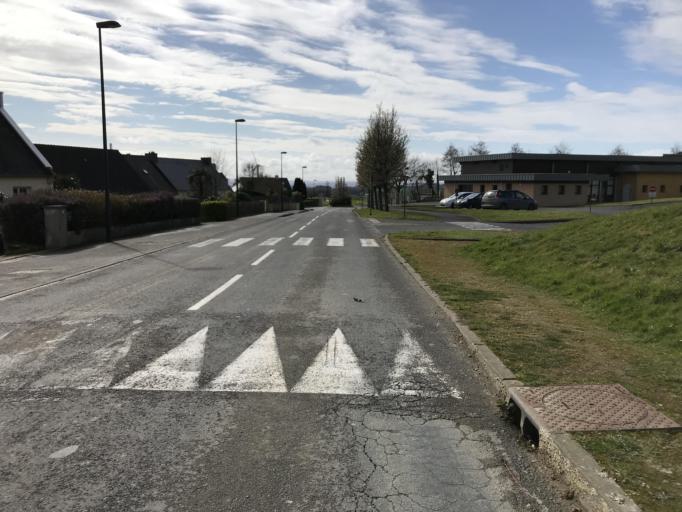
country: FR
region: Brittany
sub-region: Departement du Finistere
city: Dirinon
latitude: 48.3976
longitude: -4.2646
